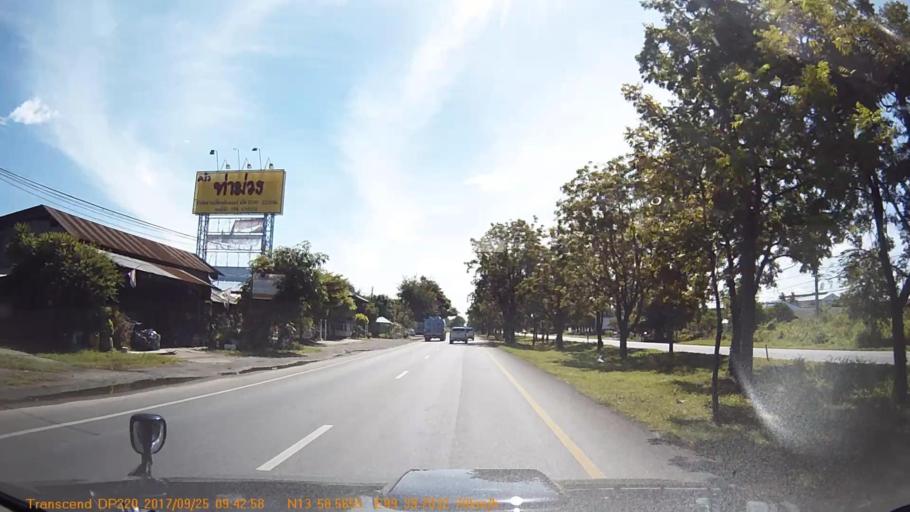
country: TH
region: Kanchanaburi
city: Tha Muang
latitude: 13.9761
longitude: 99.6620
